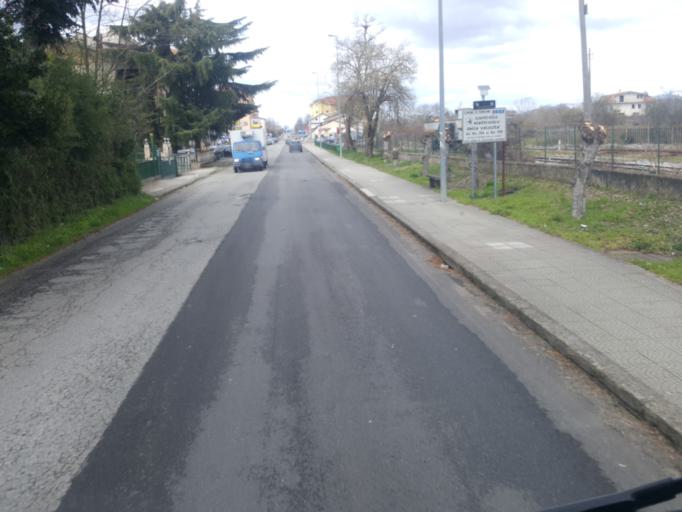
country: IT
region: Calabria
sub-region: Provincia di Cosenza
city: Santo Stefano di Rogliano
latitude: 39.2007
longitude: 16.3133
